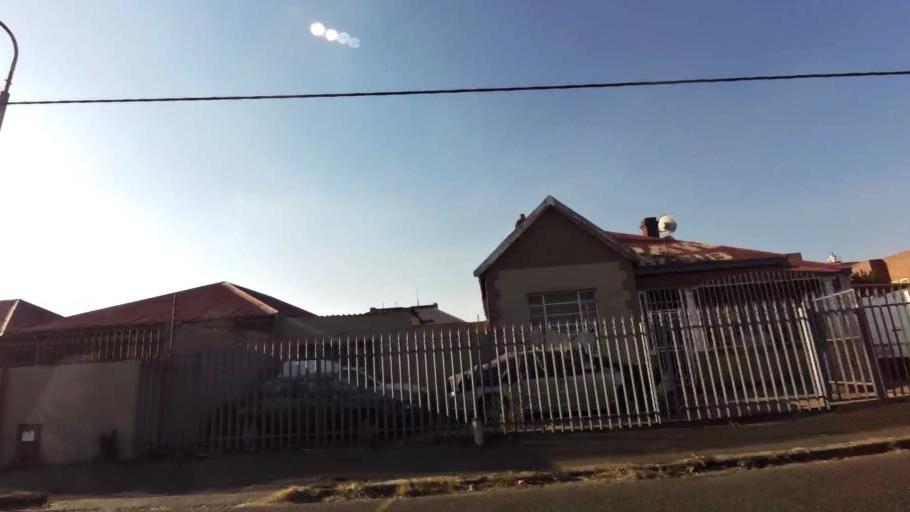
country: ZA
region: Gauteng
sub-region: City of Johannesburg Metropolitan Municipality
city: Johannesburg
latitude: -26.1930
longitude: 27.9978
